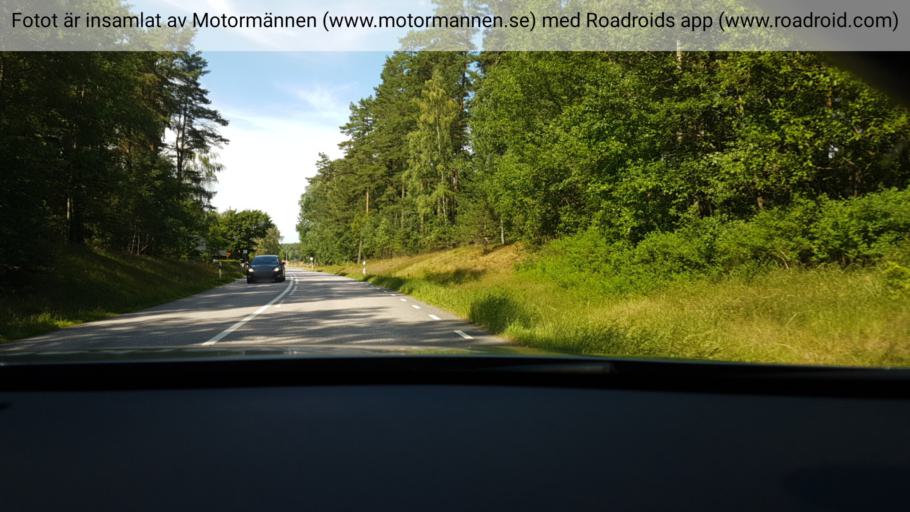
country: SE
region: Vaestra Goetaland
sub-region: Skovde Kommun
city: Stopen
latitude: 58.4680
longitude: 13.9581
